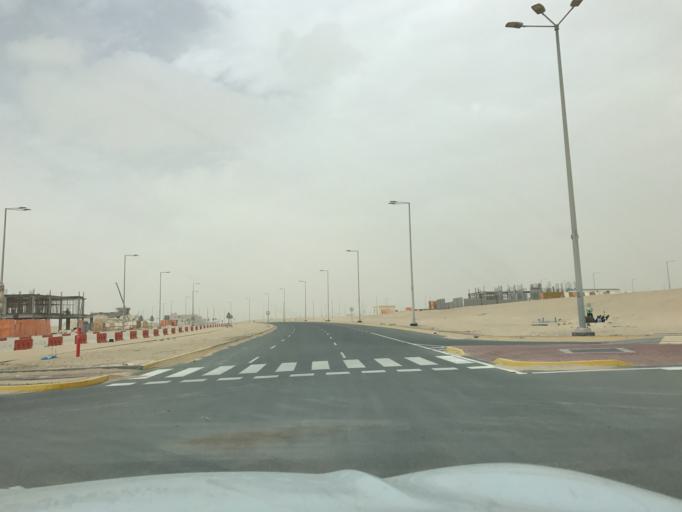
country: AE
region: Abu Dhabi
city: Abu Dhabi
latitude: 24.3449
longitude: 54.7508
